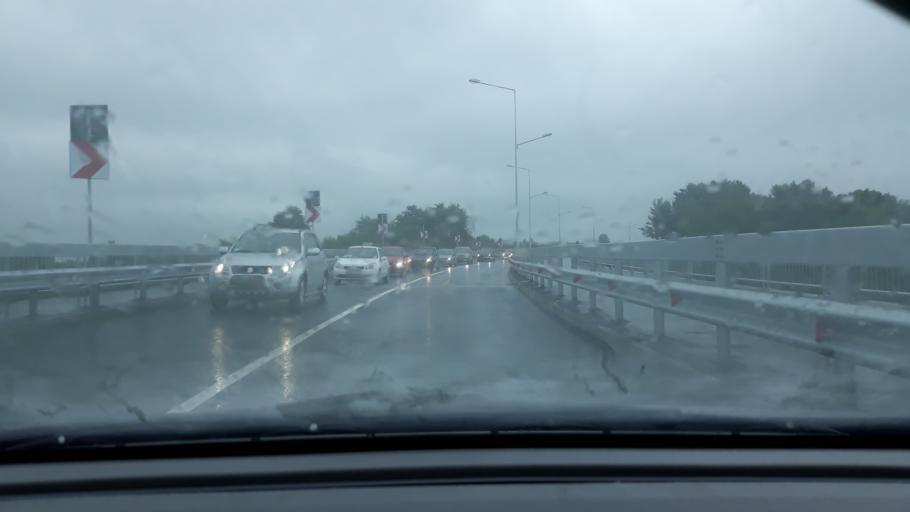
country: RO
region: Bihor
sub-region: Comuna Biharea
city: Biharea
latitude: 47.1115
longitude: 21.9034
